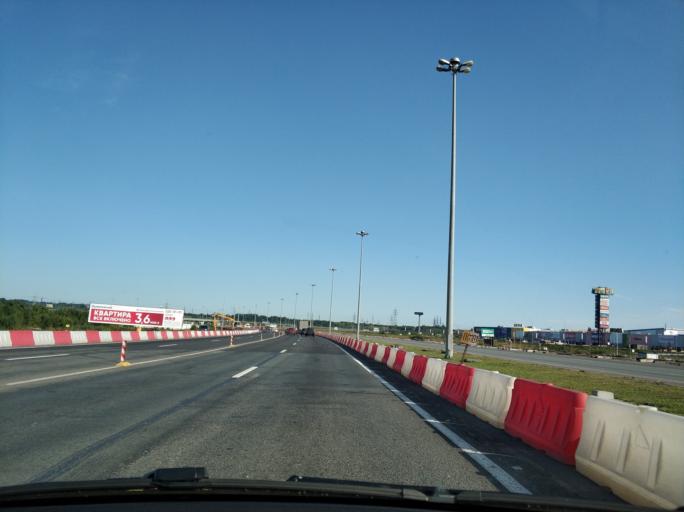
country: RU
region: Leningrad
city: Bugry
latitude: 60.0854
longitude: 30.3773
